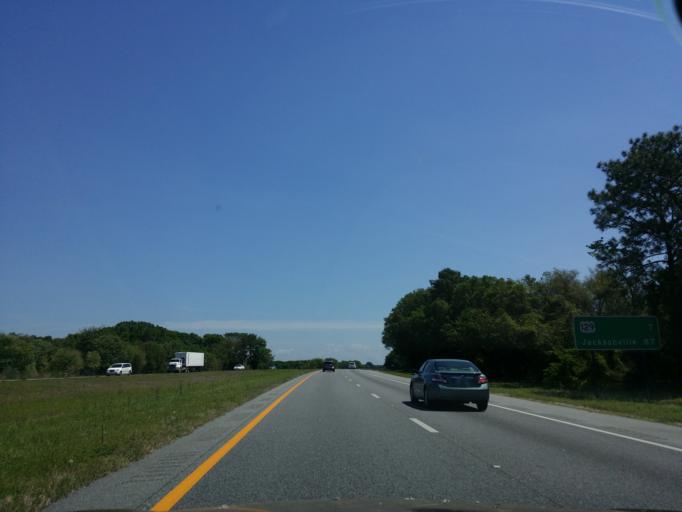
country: US
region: Florida
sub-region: Suwannee County
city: Live Oak
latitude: 30.3489
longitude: -83.0758
